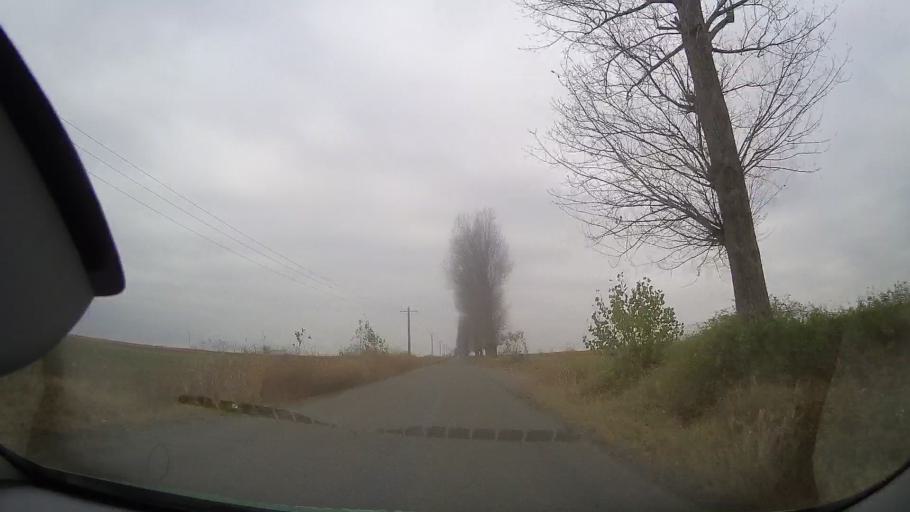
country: RO
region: Buzau
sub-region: Comuna Pogoanele
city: Pogoanele
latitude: 44.9527
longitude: 27.0162
